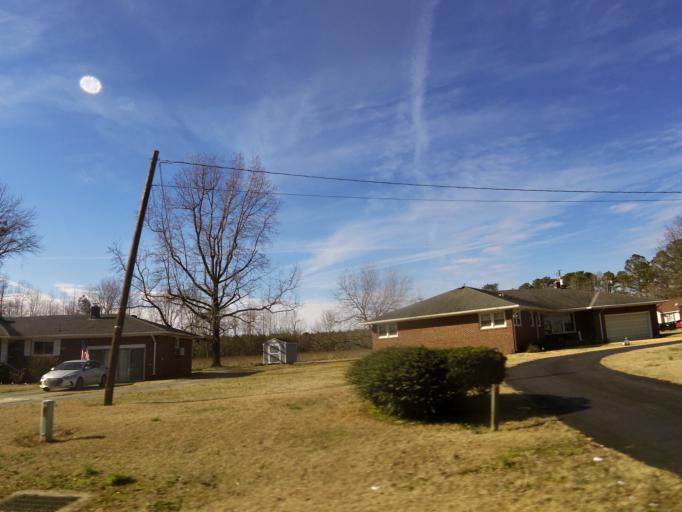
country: US
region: Virginia
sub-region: Isle of Wight County
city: Windsor
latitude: 36.8179
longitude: -76.7482
